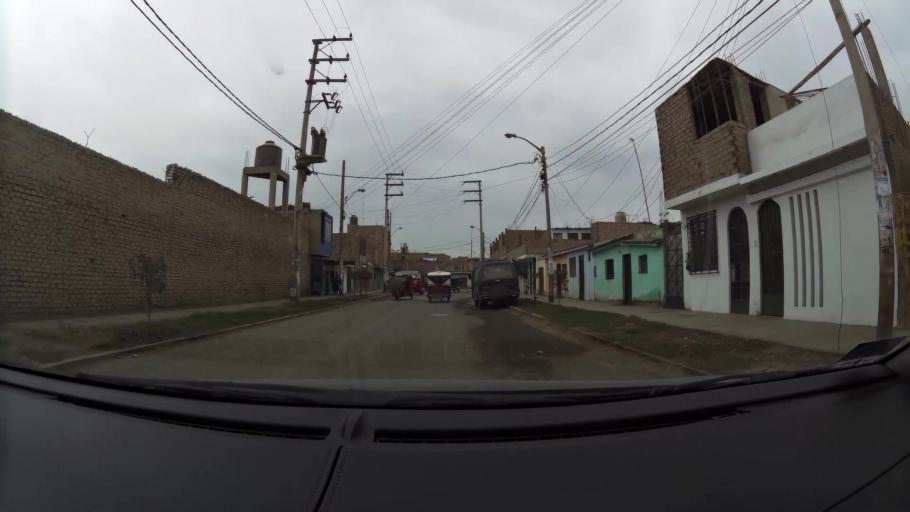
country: PE
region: Lima
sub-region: Provincia de Huaral
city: Huaral
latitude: -11.5006
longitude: -77.2123
